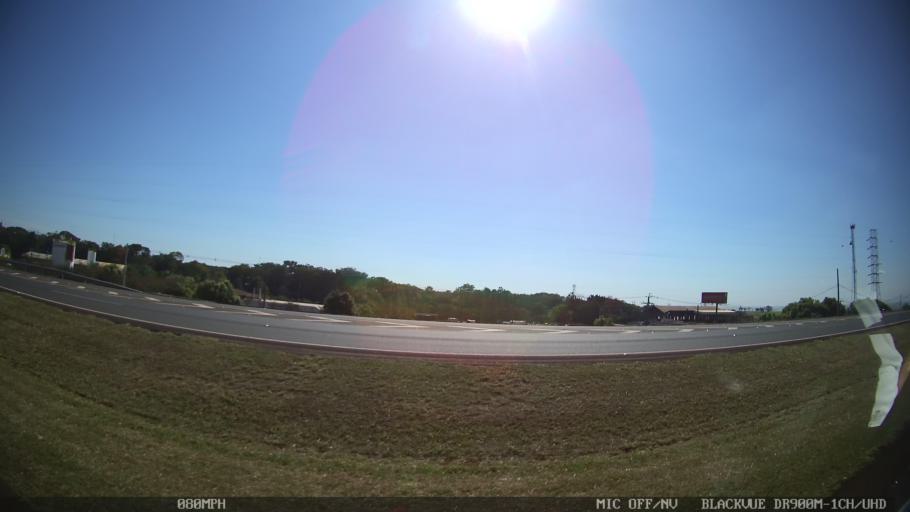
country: BR
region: Sao Paulo
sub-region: Ribeirao Preto
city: Ribeirao Preto
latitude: -21.1463
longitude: -47.8780
